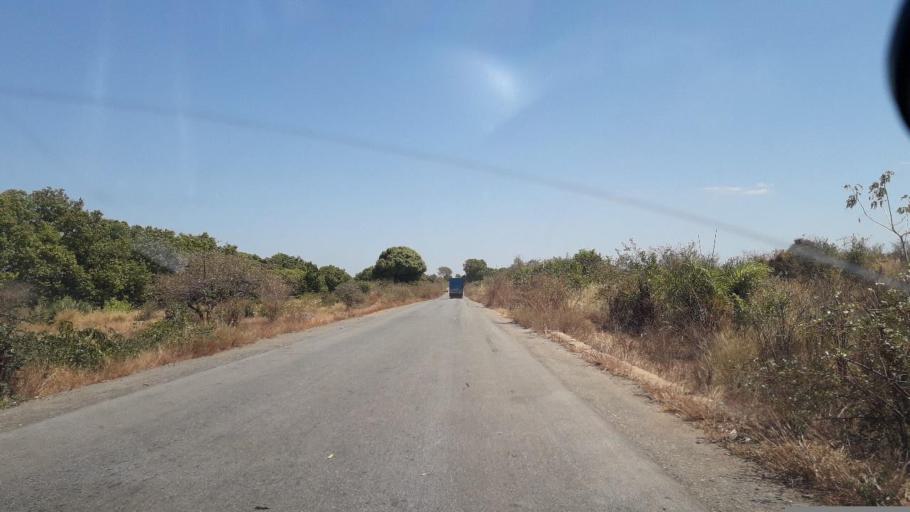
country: MG
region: Betsiboka
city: Maevatanana
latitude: -16.7599
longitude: 47.0432
